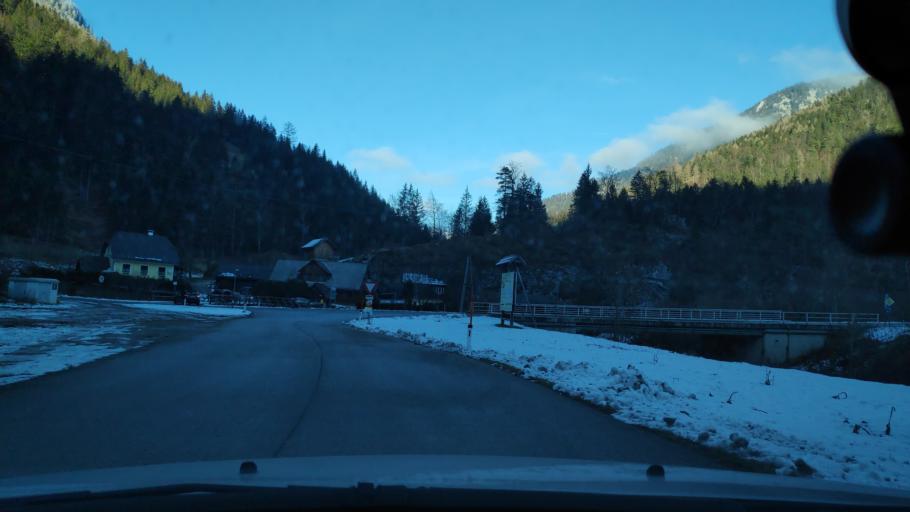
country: AT
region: Lower Austria
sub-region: Politischer Bezirk Neunkirchen
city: Schwarzau im Gebirge
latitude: 47.7724
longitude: 15.7307
